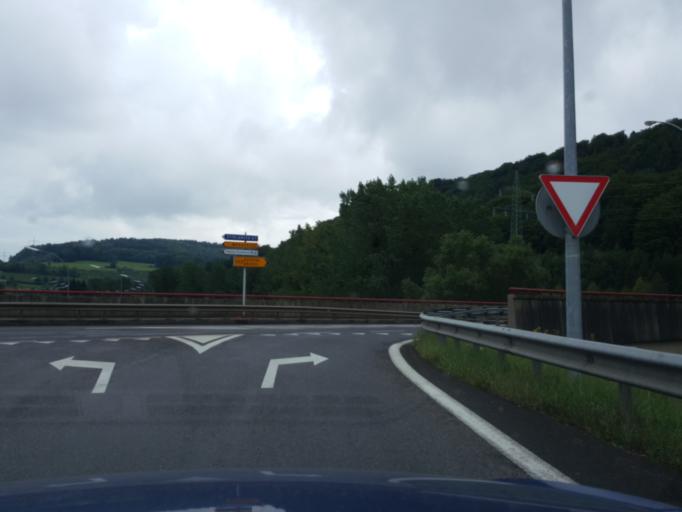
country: LU
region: Luxembourg
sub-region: Canton de Mersch
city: Mersch
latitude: 49.7370
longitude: 6.0974
